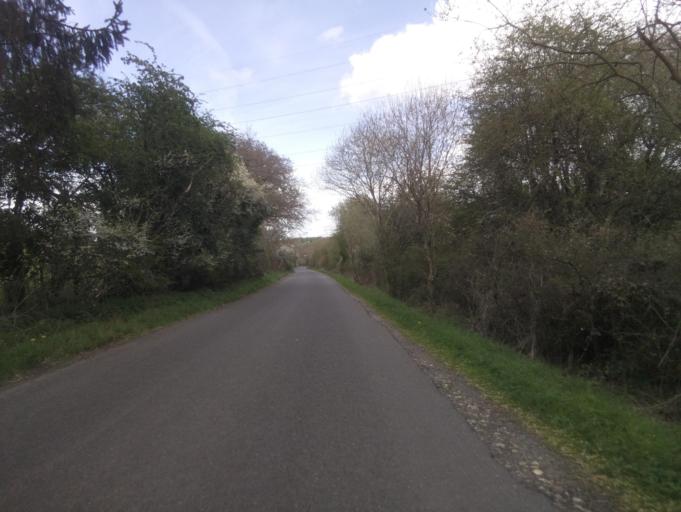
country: GB
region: England
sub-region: Hampshire
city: Highclere
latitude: 51.2864
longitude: -1.4445
